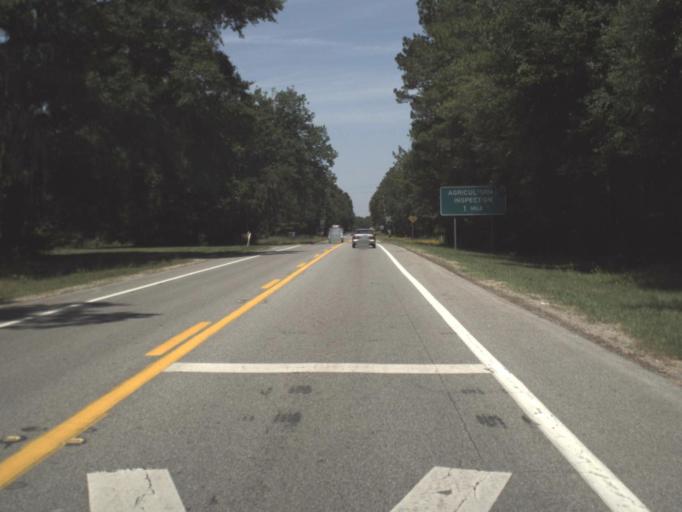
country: US
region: Florida
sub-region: Suwannee County
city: Live Oak
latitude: 30.3745
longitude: -83.1594
